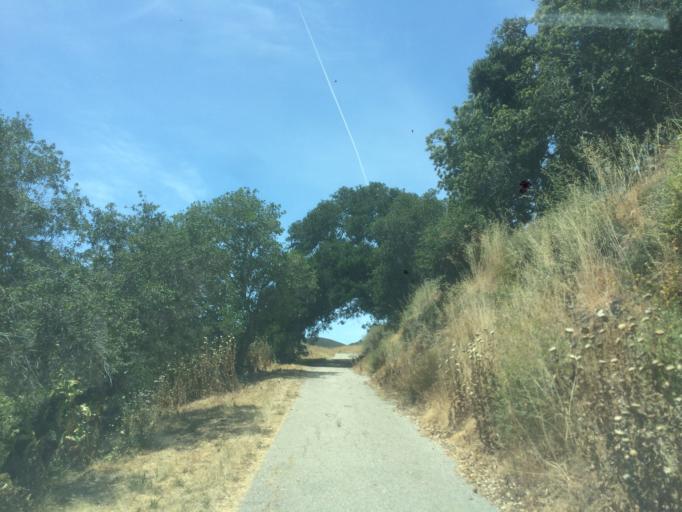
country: US
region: California
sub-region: San Luis Obispo County
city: San Luis Obispo
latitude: 35.2547
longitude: -120.7009
